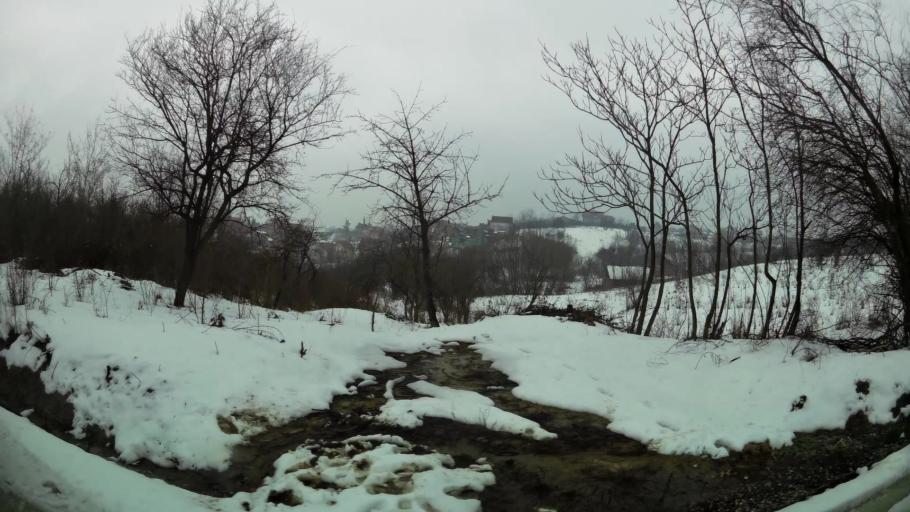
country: RS
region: Central Serbia
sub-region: Belgrade
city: Zvezdara
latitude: 44.7500
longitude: 20.5226
